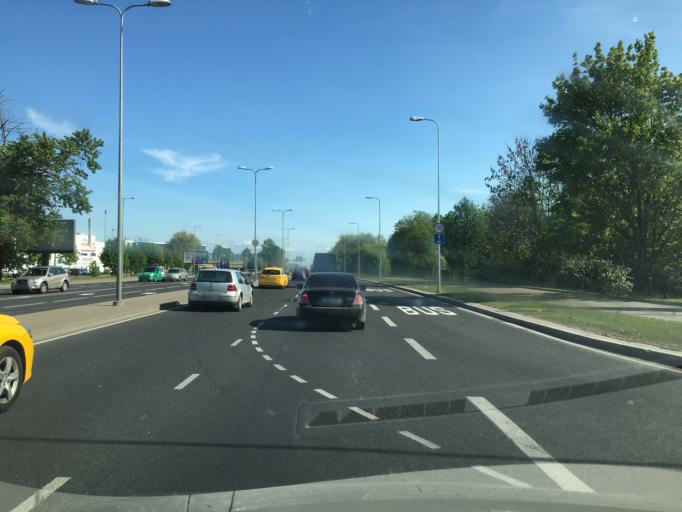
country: EE
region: Harju
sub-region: Tallinna linn
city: Tallinn
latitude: 59.4221
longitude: 24.7883
